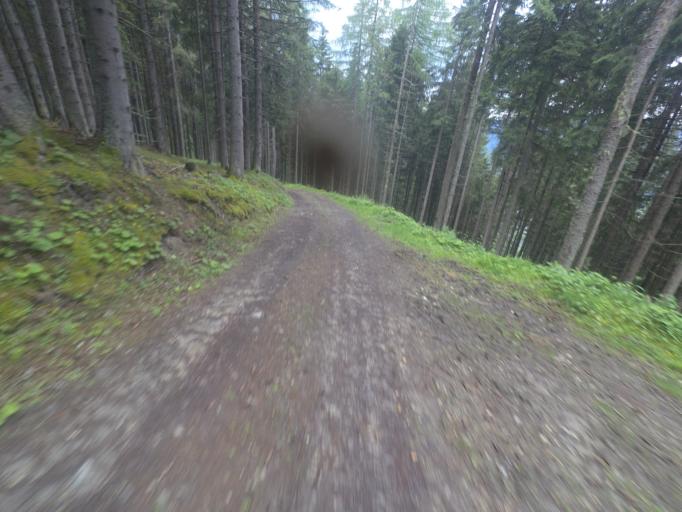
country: AT
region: Salzburg
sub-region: Politischer Bezirk Sankt Johann im Pongau
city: Schwarzach im Pongau
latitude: 47.3078
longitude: 13.1611
